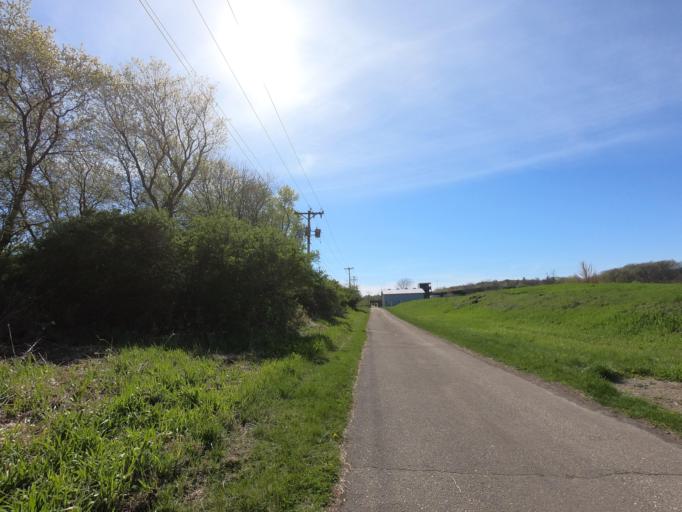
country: US
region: Wisconsin
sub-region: Dane County
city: Middleton
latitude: 43.1040
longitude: -89.5336
